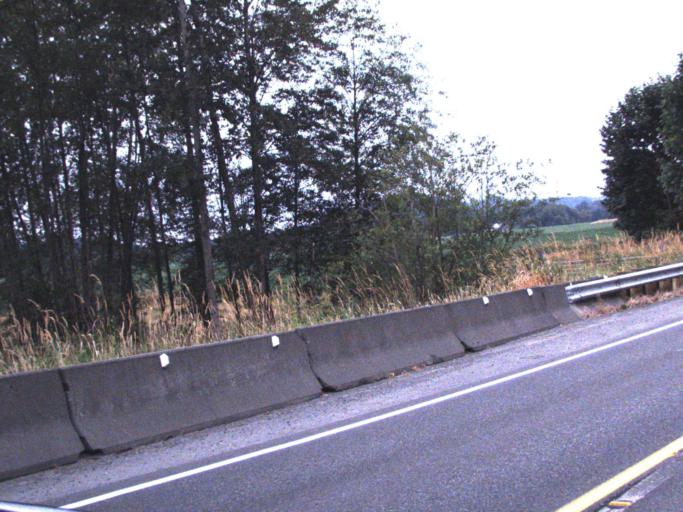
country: US
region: Washington
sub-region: Snohomish County
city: Monroe
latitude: 47.8014
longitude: -121.9794
